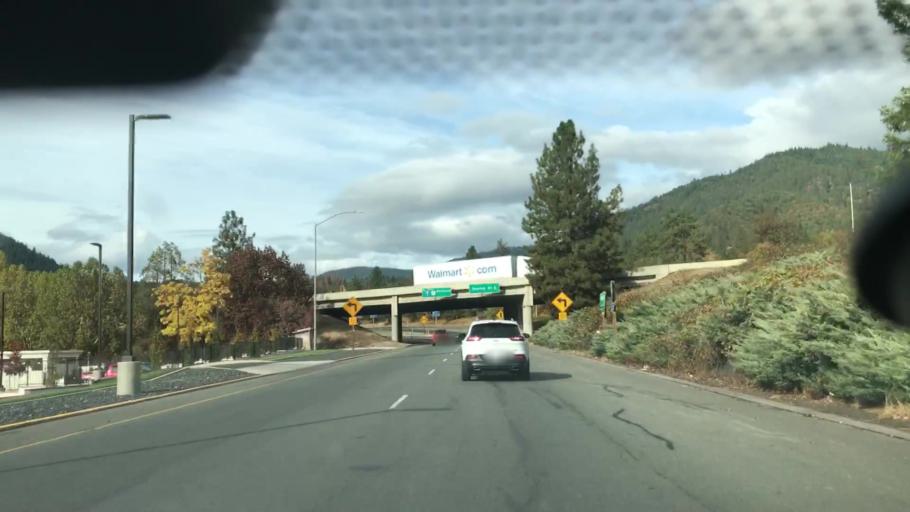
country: US
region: Oregon
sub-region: Josephine County
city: Grants Pass
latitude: 42.4625
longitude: -123.3207
